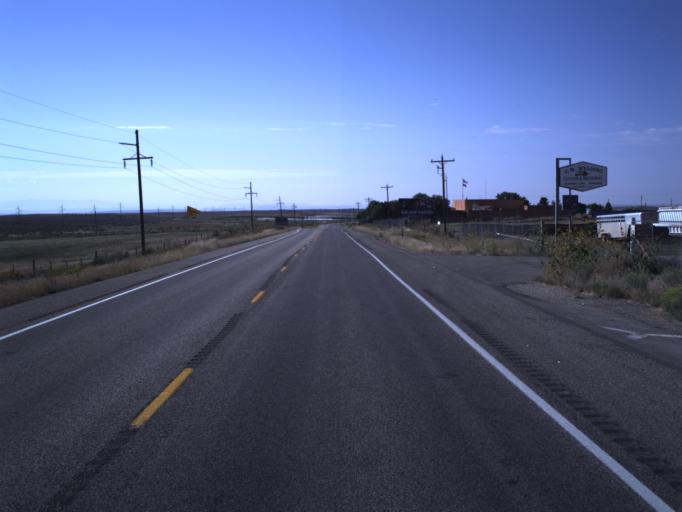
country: US
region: Utah
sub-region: San Juan County
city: Blanding
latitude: 37.5844
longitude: -109.4783
